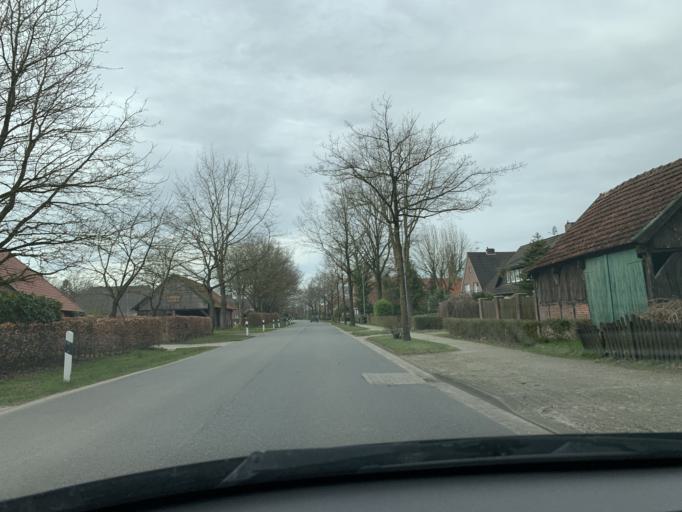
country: DE
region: Lower Saxony
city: Bad Zwischenahn
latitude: 53.1596
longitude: 7.9900
